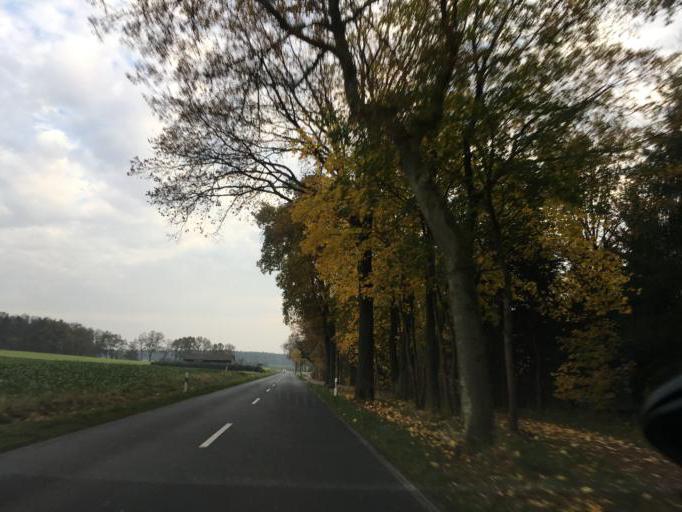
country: DE
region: Lower Saxony
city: Wietzendorf
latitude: 52.8990
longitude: 9.9834
